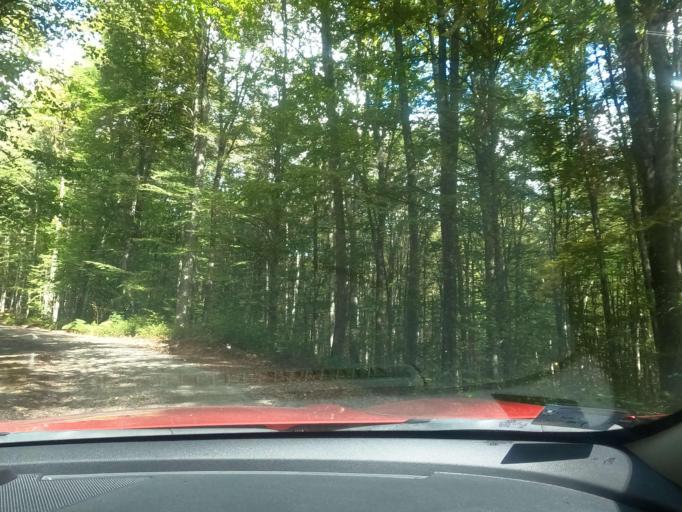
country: BA
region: Federation of Bosnia and Herzegovina
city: Velika Kladusa
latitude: 45.2481
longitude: 15.7729
